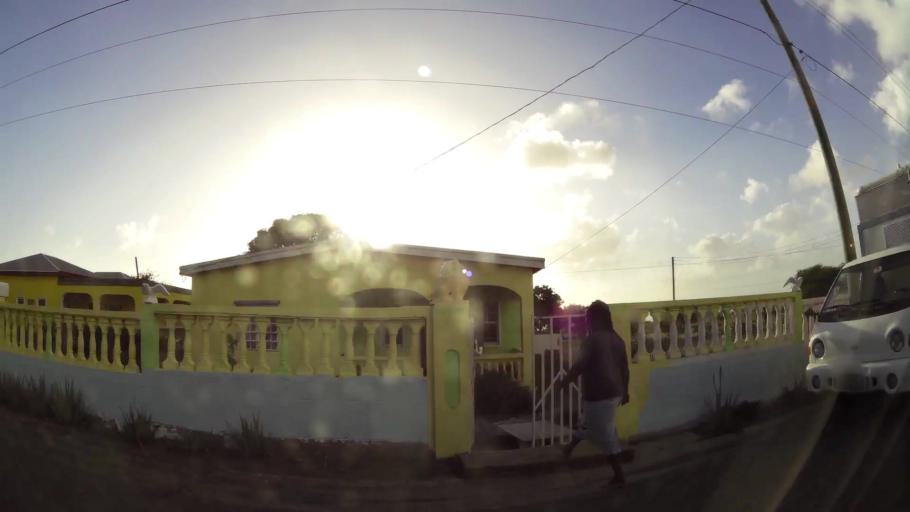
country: KN
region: Saint John Figtree
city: Fig Tree
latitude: 17.1182
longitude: -62.6056
